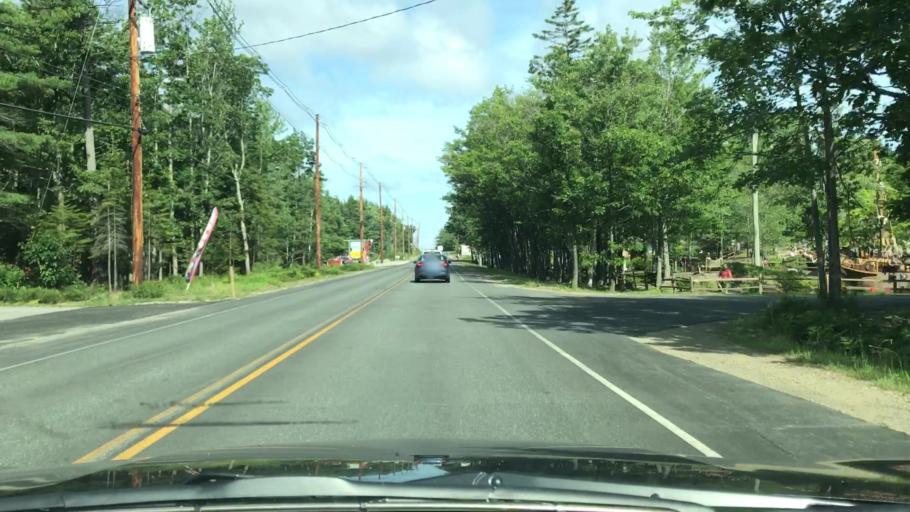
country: US
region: Maine
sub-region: Hancock County
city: Bar Harbor
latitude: 44.4308
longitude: -68.2693
